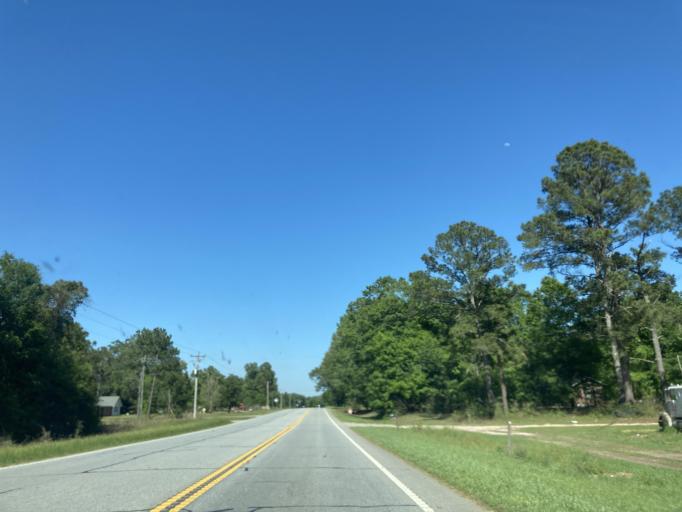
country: US
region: Georgia
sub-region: Baker County
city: Newton
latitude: 31.2893
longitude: -84.3579
